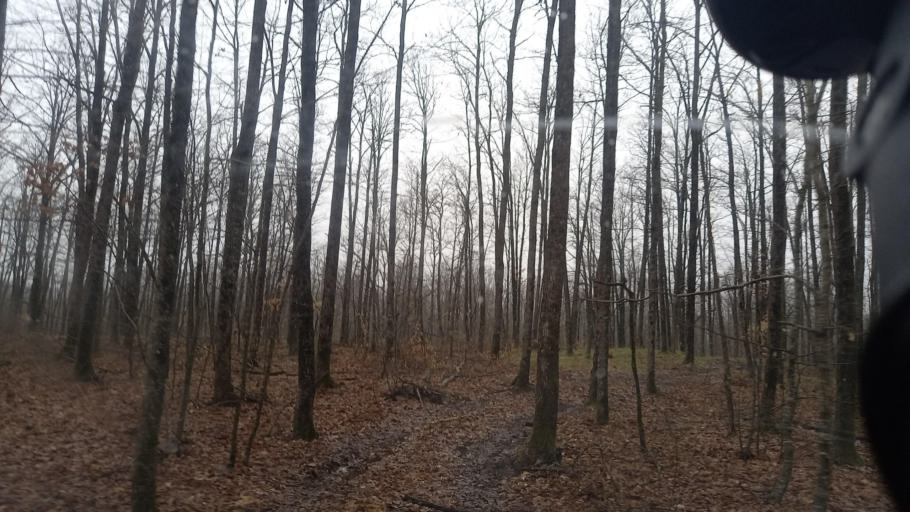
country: RU
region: Krasnodarskiy
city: Saratovskaya
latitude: 44.6479
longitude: 39.2461
